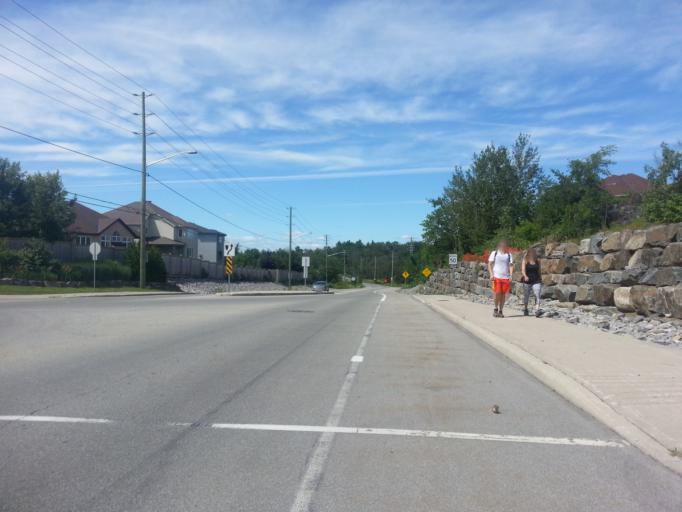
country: CA
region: Ontario
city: Bells Corners
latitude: 45.3256
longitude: -75.9294
